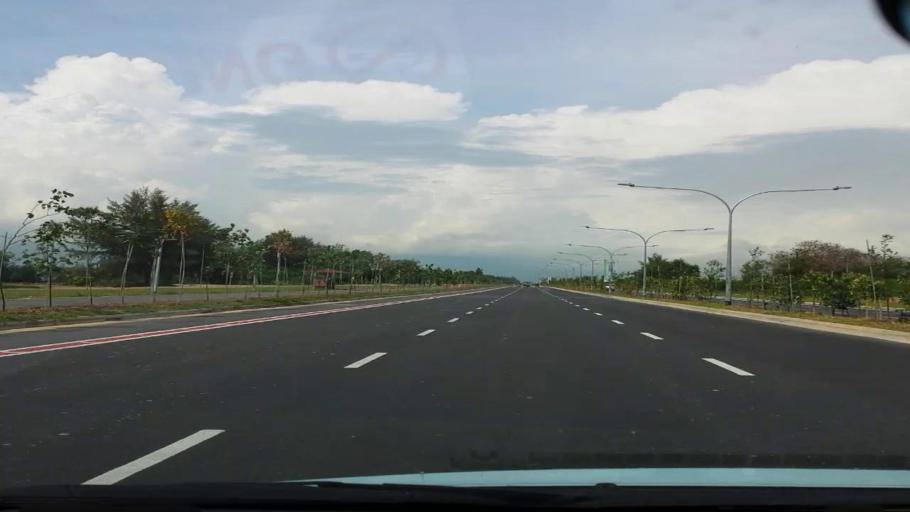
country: SG
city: Singapore
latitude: 1.3526
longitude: 104.0302
